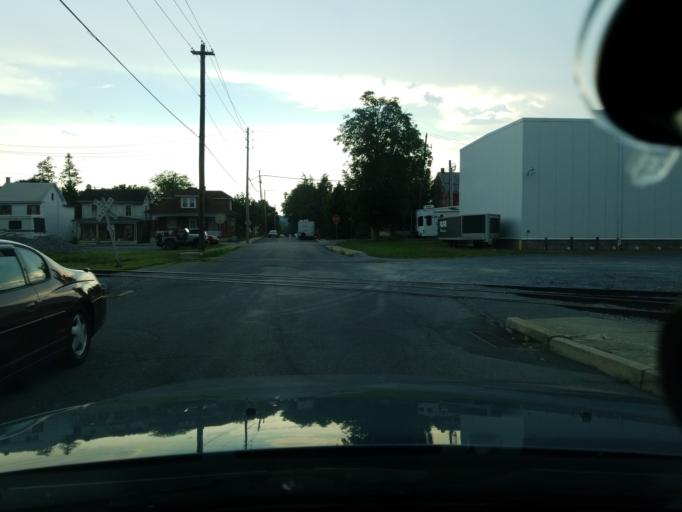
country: US
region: Pennsylvania
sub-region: Dauphin County
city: Hummelstown
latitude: 40.2659
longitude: -76.7164
